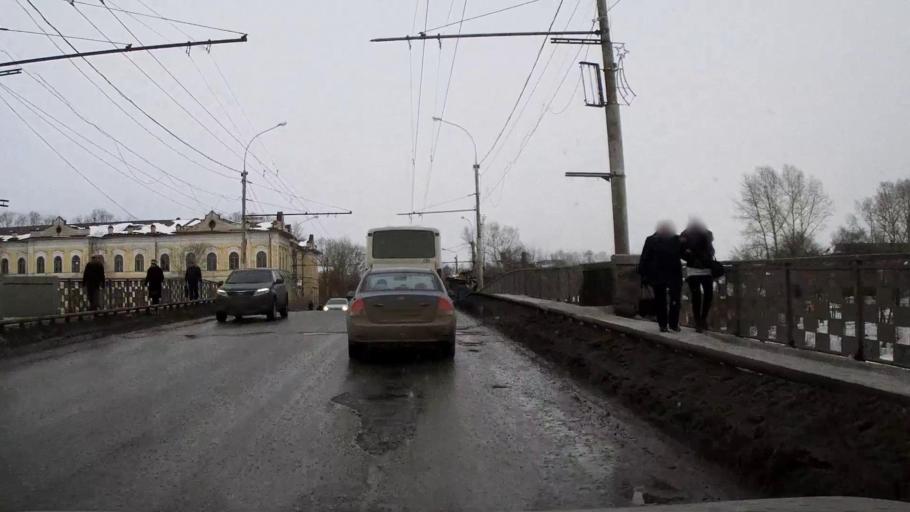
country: RU
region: Vologda
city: Vologda
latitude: 59.2236
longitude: 39.8911
